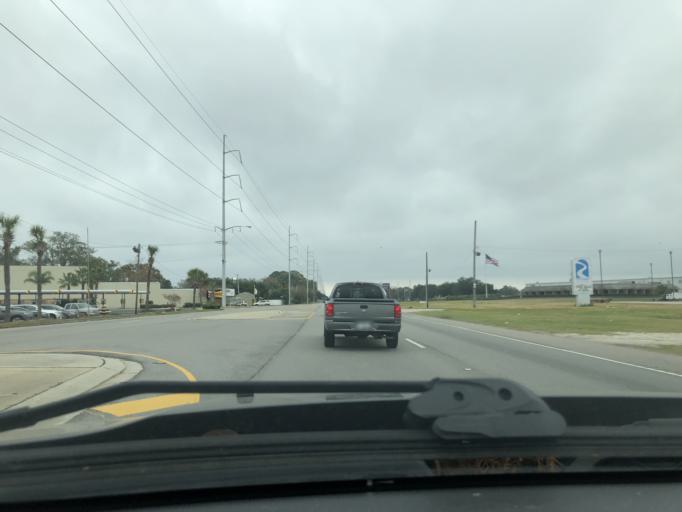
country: US
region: Louisiana
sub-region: Jefferson Parish
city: Elmwood
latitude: 29.9766
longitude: -90.1951
